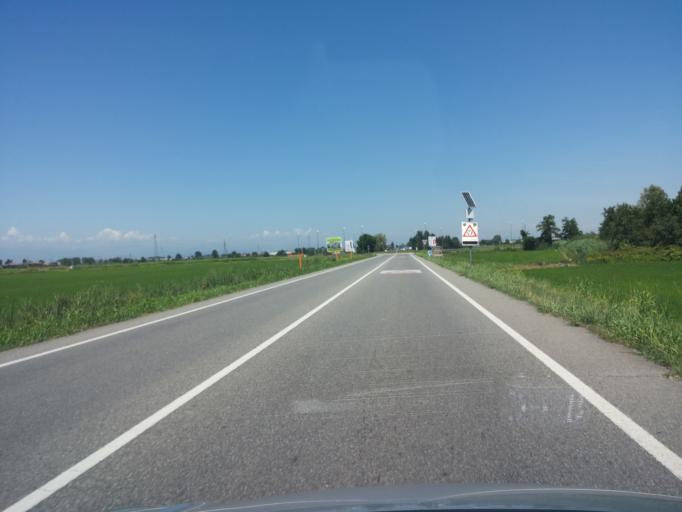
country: IT
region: Piedmont
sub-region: Provincia di Vercelli
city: Caresanablot
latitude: 45.3327
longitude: 8.3910
